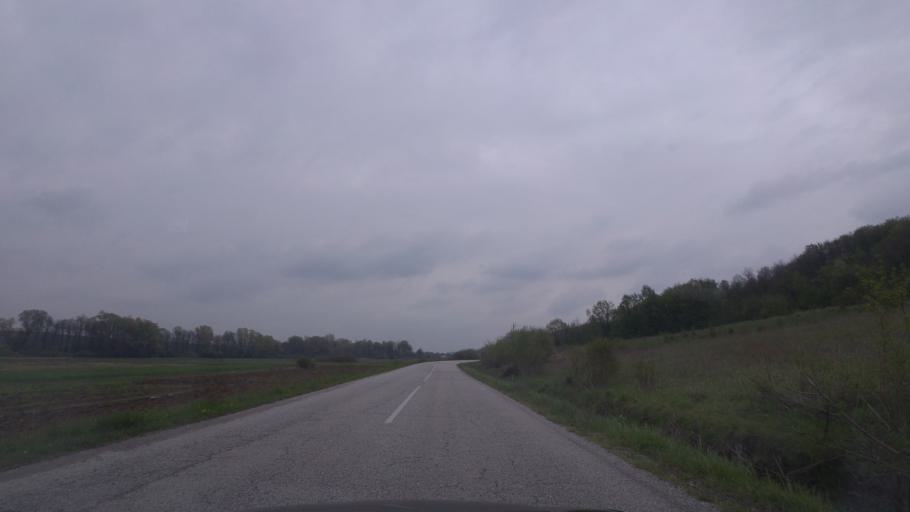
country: HR
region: Karlovacka
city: Ozalj
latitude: 45.6431
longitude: 15.5292
